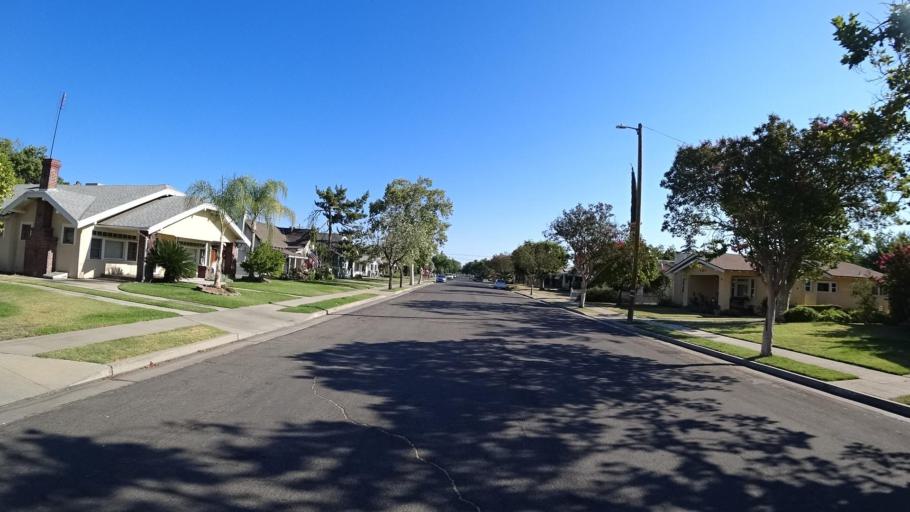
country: US
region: California
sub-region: Fresno County
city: Fresno
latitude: 36.7586
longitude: -119.8143
